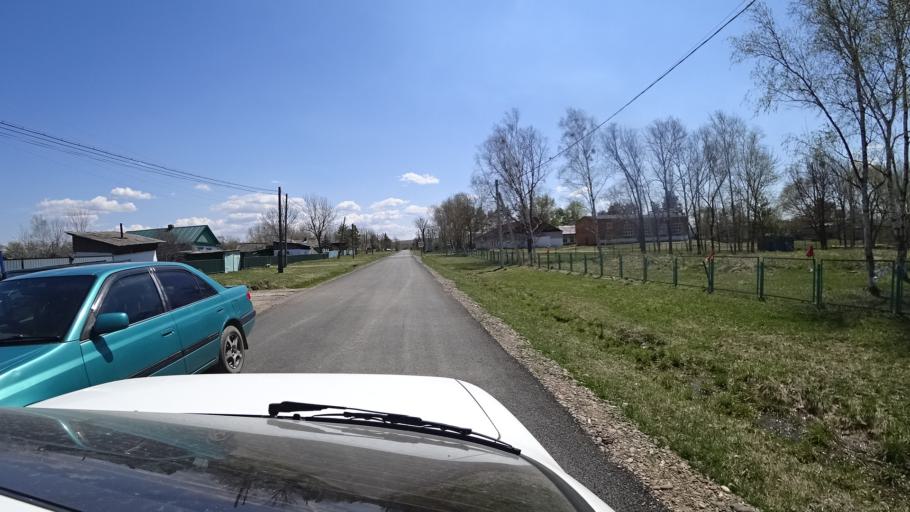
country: RU
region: Primorskiy
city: Dal'nerechensk
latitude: 45.7958
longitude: 133.7680
